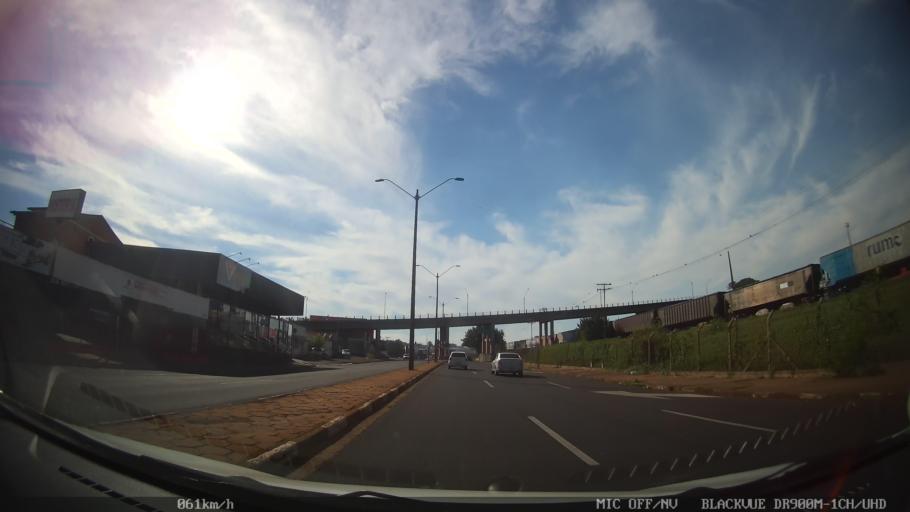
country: BR
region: Sao Paulo
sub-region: Araraquara
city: Araraquara
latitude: -21.7875
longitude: -48.1722
